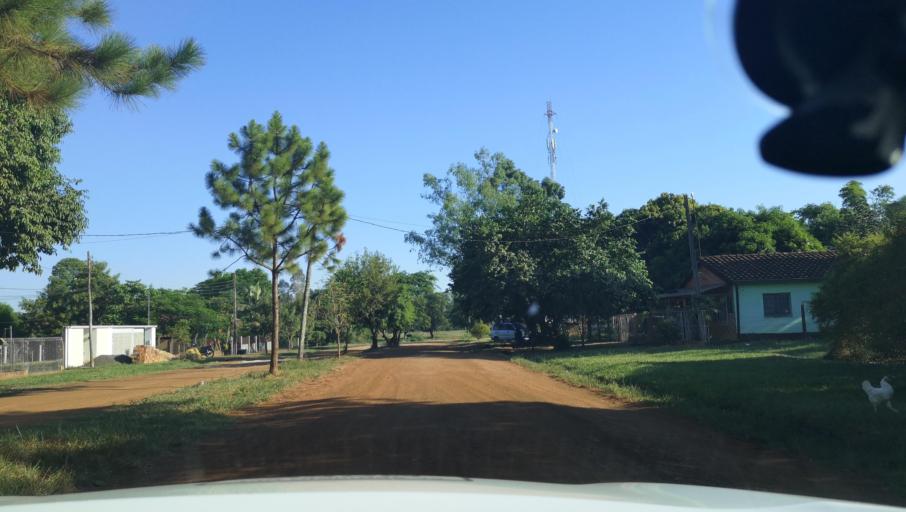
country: PY
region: Itapua
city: Carmen del Parana
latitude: -27.1550
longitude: -56.2427
